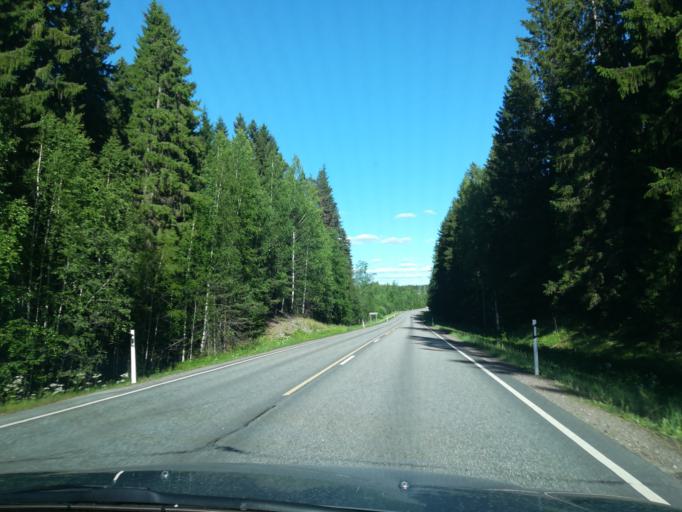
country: FI
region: South Karelia
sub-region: Imatra
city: Ruokolahti
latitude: 61.3509
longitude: 28.7429
